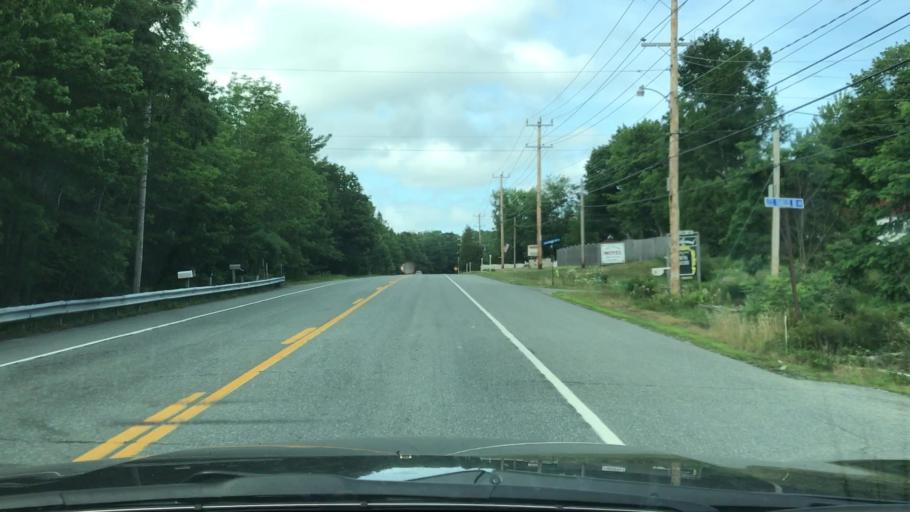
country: US
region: Maine
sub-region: Hancock County
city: Trenton
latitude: 44.4298
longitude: -68.3227
